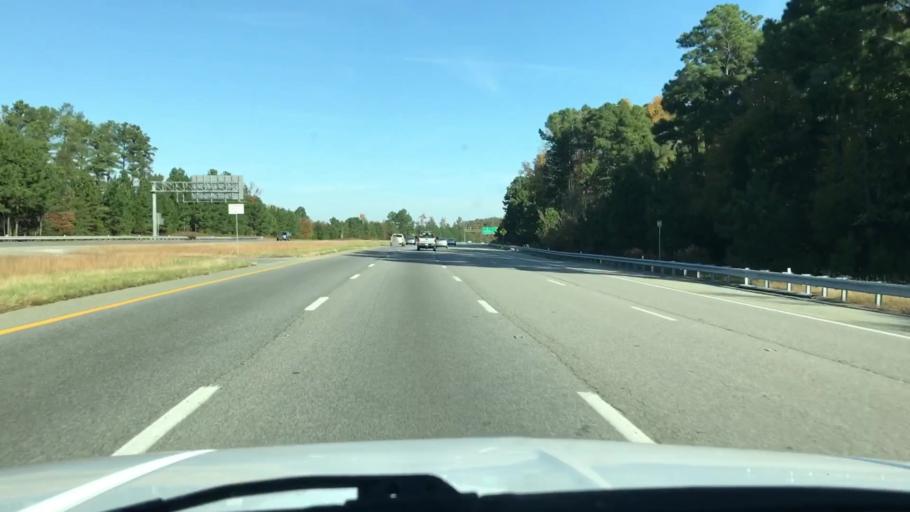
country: US
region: Virginia
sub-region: Henrico County
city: Short Pump
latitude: 37.6434
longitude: -77.6651
